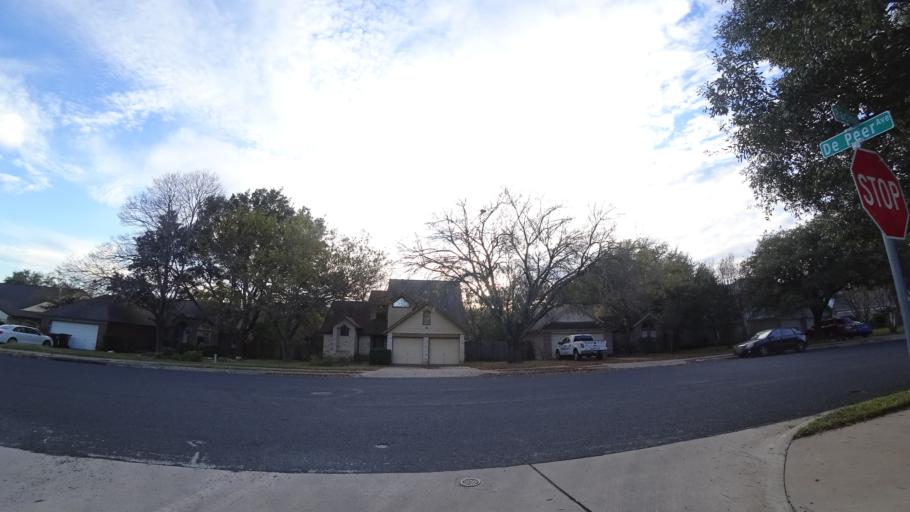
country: US
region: Texas
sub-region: Williamson County
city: Brushy Creek
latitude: 30.4912
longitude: -97.7410
